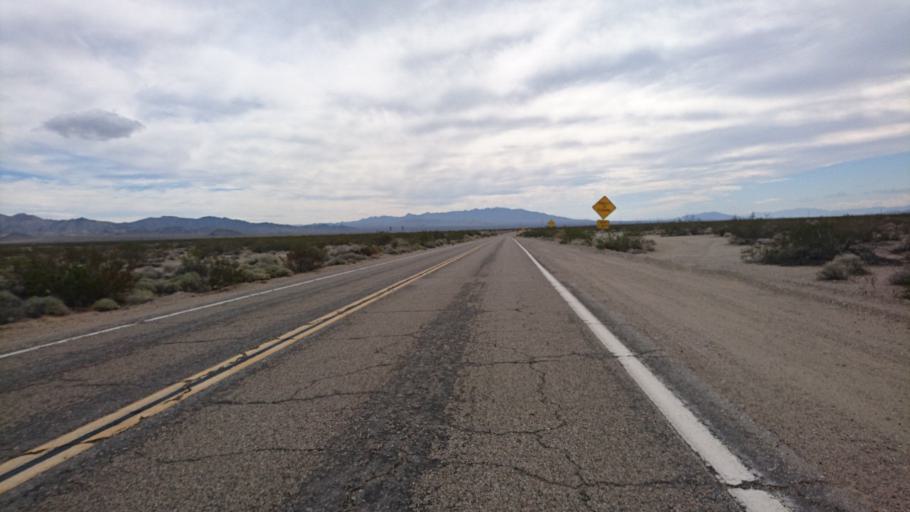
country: US
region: California
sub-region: San Bernardino County
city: Needles
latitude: 34.8099
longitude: -115.1907
